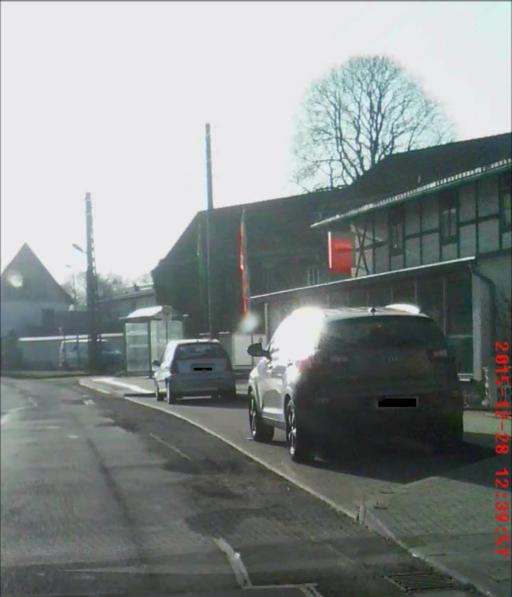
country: DE
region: Thuringia
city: Ossmanstedt
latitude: 51.0121
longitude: 11.4238
